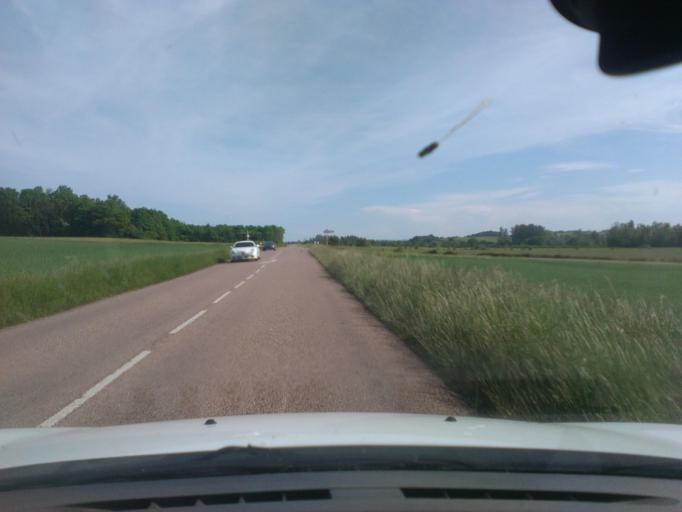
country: FR
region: Lorraine
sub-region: Departement des Vosges
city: Rambervillers
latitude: 48.4015
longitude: 6.5895
